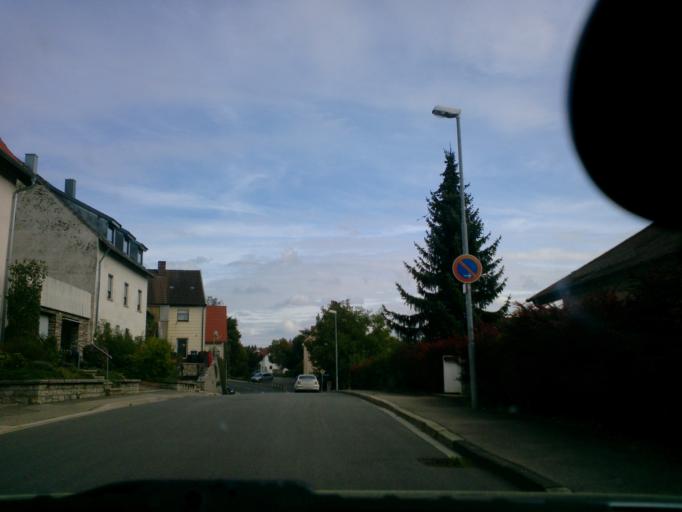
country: DE
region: Baden-Wuerttemberg
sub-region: Regierungsbezirk Stuttgart
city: Gemmingen
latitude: 49.1467
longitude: 8.9647
